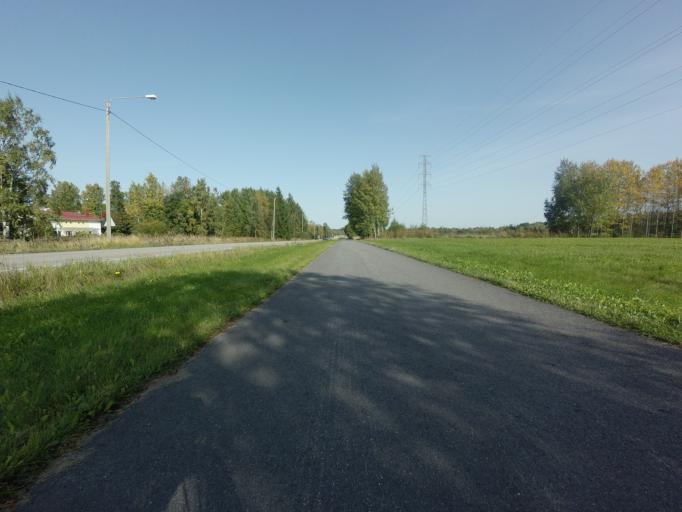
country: FI
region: Uusimaa
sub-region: Helsinki
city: Espoo
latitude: 60.1722
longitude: 24.6593
